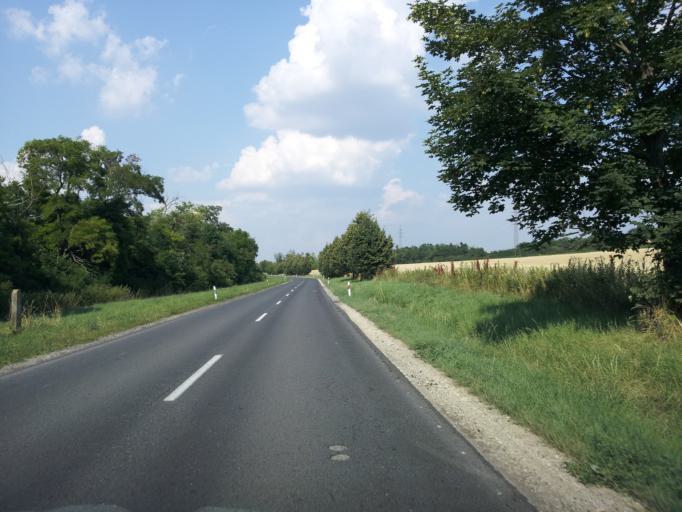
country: HU
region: Veszprem
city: Nemesvamos
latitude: 47.0263
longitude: 17.8038
